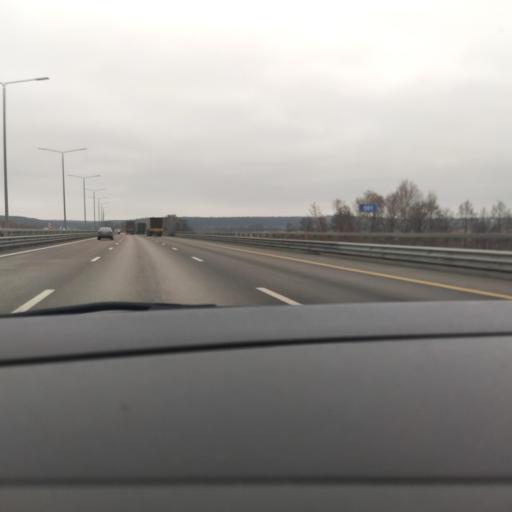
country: RU
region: Voronezj
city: Somovo
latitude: 51.7868
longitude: 39.2831
